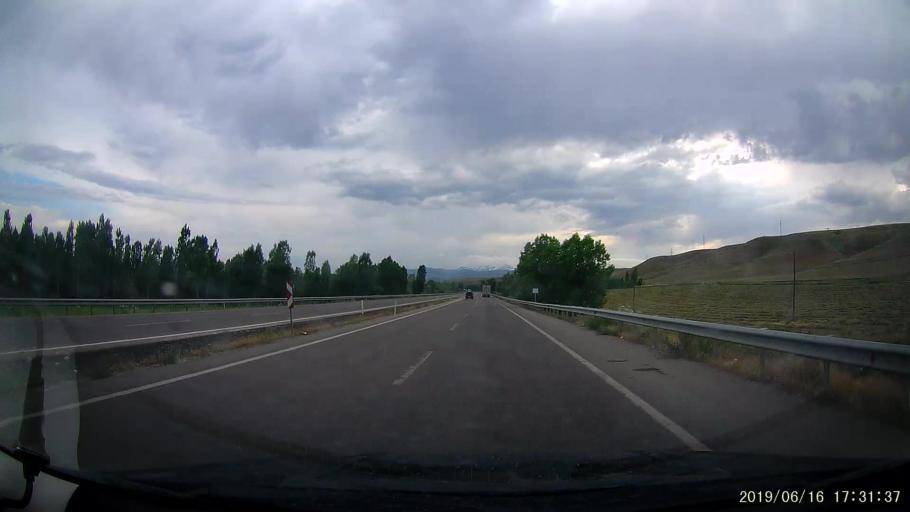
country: TR
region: Erzincan
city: Tercan
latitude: 39.7727
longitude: 40.3187
